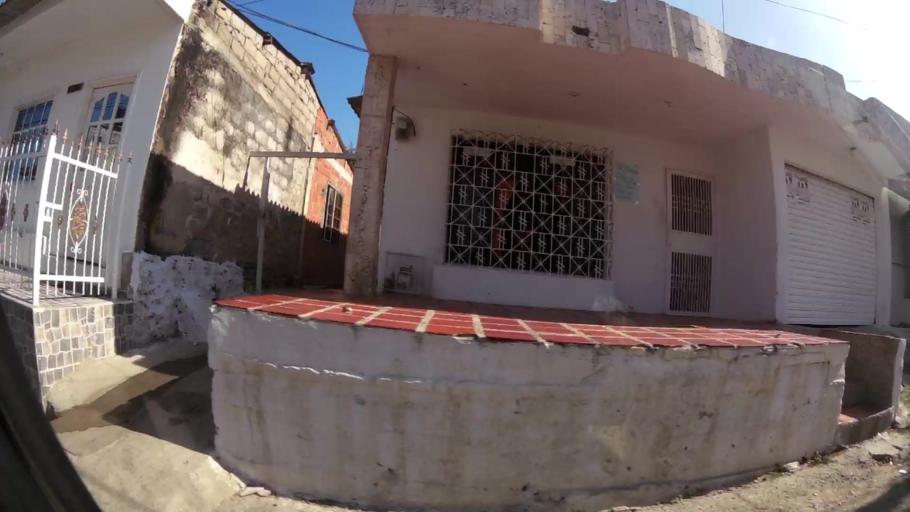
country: CO
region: Bolivar
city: Cartagena
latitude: 10.4244
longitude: -75.5366
